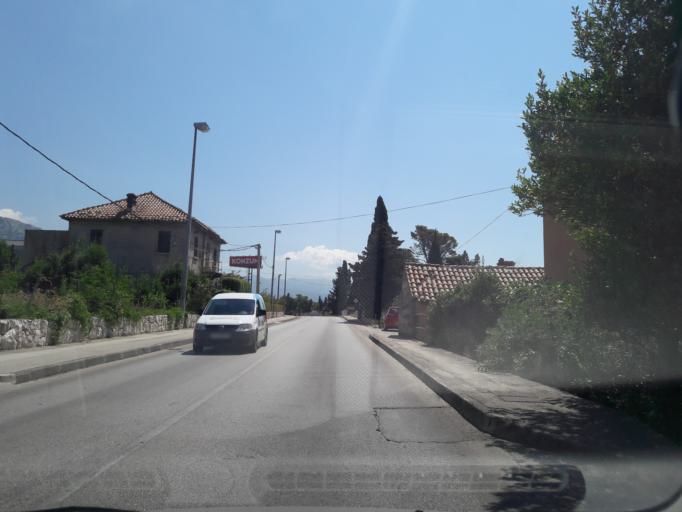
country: HR
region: Splitsko-Dalmatinska
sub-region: Grad Split
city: Split
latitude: 43.5472
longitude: 16.4058
